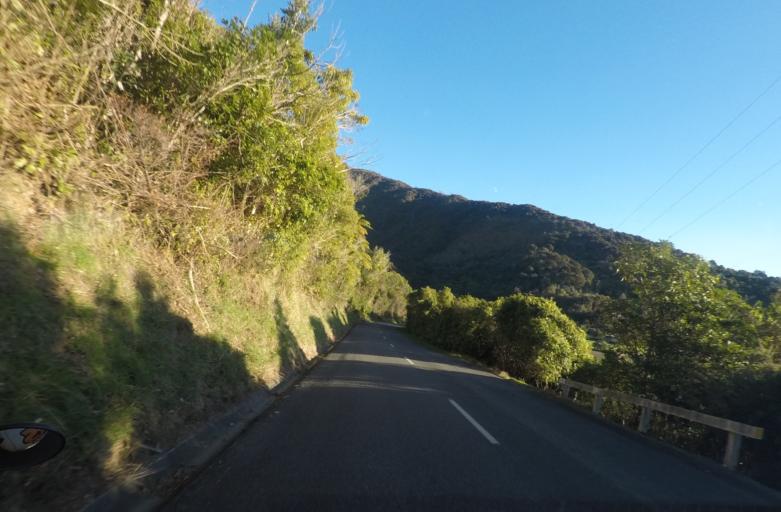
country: NZ
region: Marlborough
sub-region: Marlborough District
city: Picton
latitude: -41.2693
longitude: 173.9434
